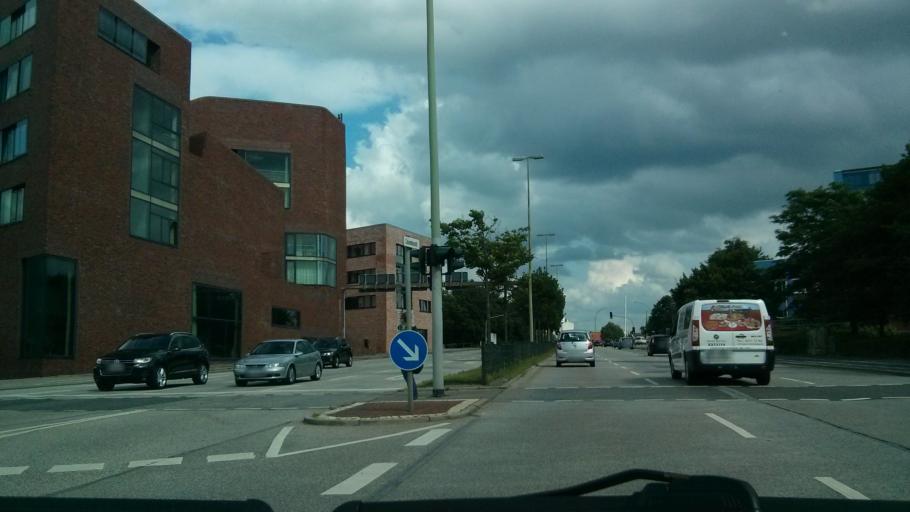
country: DE
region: Bremen
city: Bremerhaven
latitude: 53.5397
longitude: 8.5808
